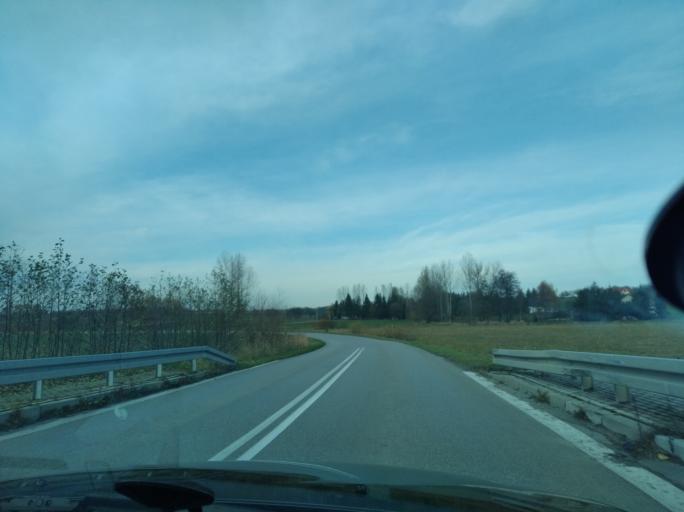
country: PL
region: Subcarpathian Voivodeship
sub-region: Powiat lancucki
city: Albigowa
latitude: 50.0359
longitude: 22.2201
